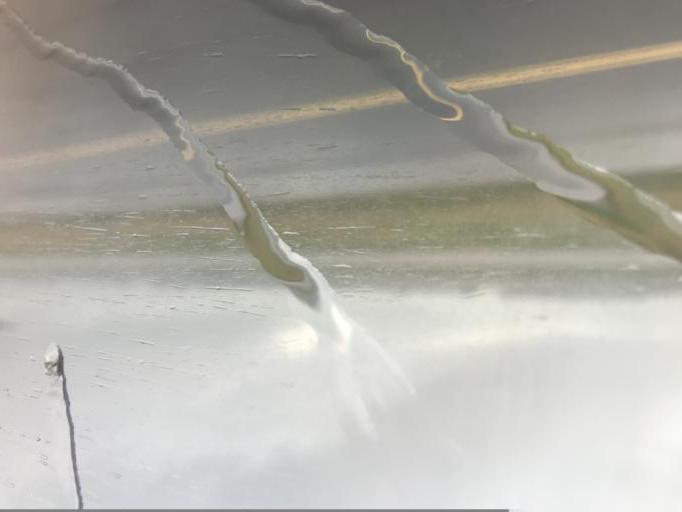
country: IT
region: Latium
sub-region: Citta metropolitana di Roma Capitale
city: Npp 23 (Parco Leonardo)
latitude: 41.8231
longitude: 12.2679
